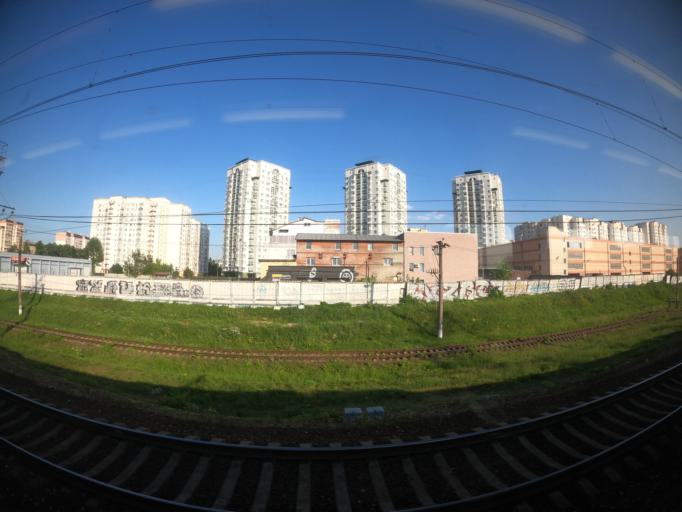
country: RU
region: Moscow
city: Ochakovo-Matveyevskoye
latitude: 55.6801
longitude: 37.4450
